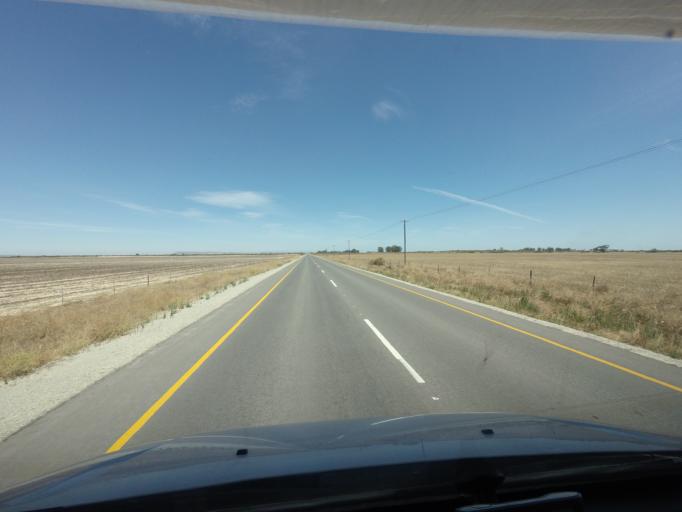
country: ZA
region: Western Cape
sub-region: West Coast District Municipality
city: Vredenburg
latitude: -32.7968
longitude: 18.2628
